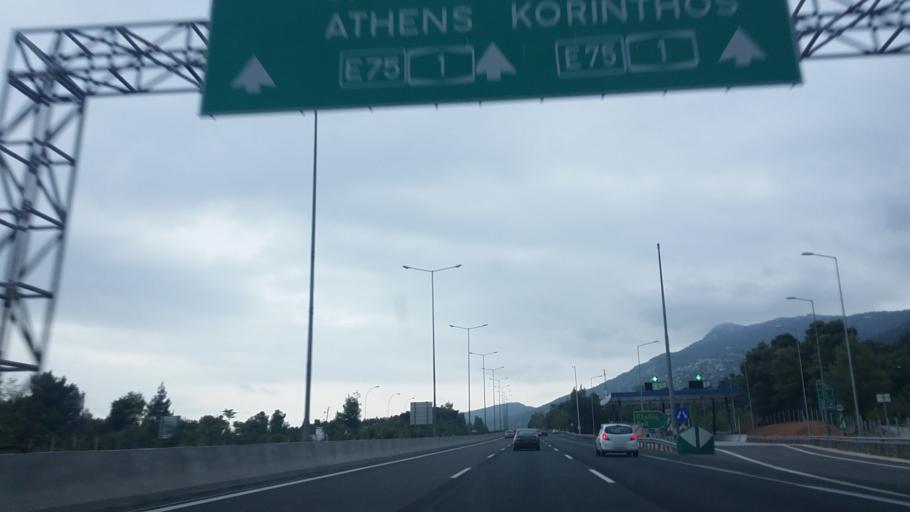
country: GR
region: Attica
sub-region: Nomarchia Anatolikis Attikis
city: Markopoulo Oropou
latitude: 38.2382
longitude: 23.7791
